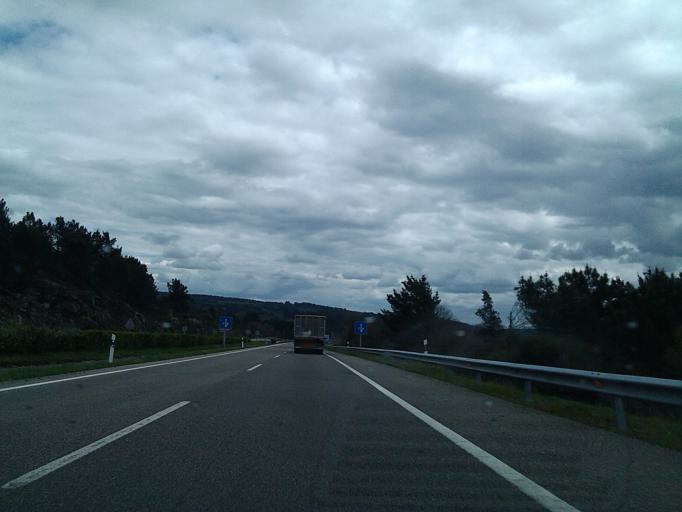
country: ES
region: Galicia
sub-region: Provincia de Lugo
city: Guitiriz
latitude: 43.1858
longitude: -7.8356
